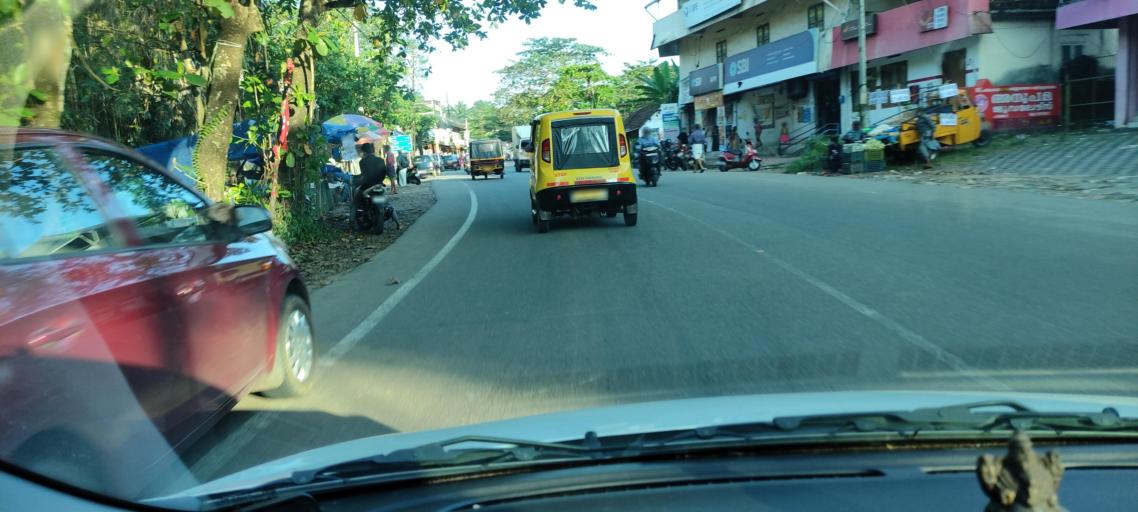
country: IN
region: Kerala
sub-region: Pattanamtitta
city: Adur
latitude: 9.1485
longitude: 76.7589
